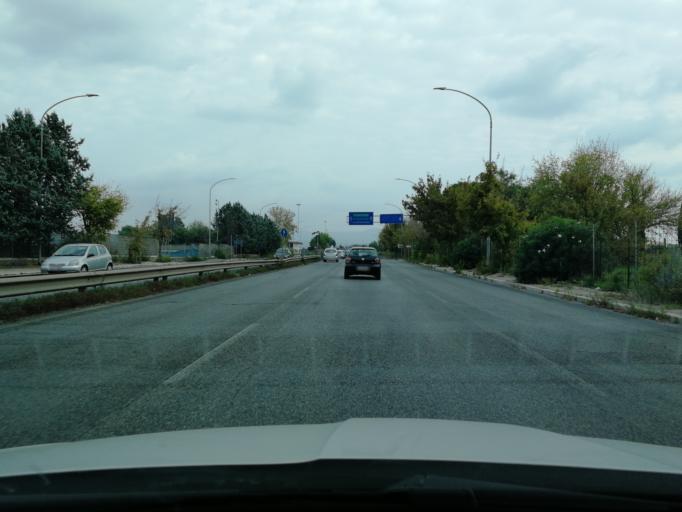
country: IT
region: Latium
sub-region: Citta metropolitana di Roma Capitale
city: Ciampino
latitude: 41.8455
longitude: 12.5800
